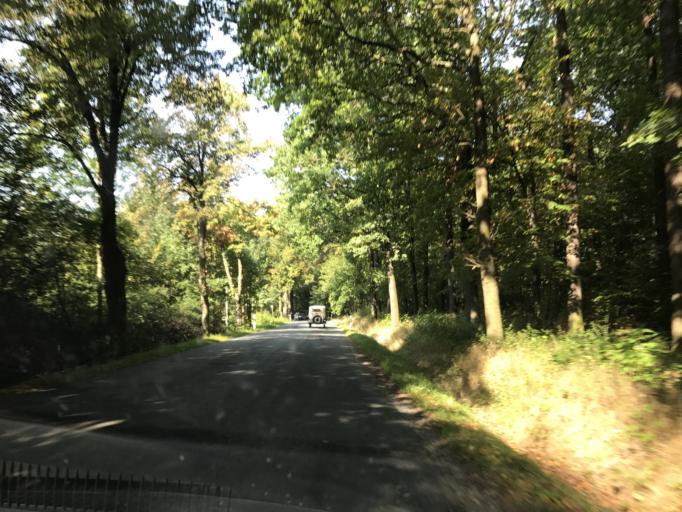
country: DE
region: Saxony
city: Lobau
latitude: 51.0881
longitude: 14.6807
